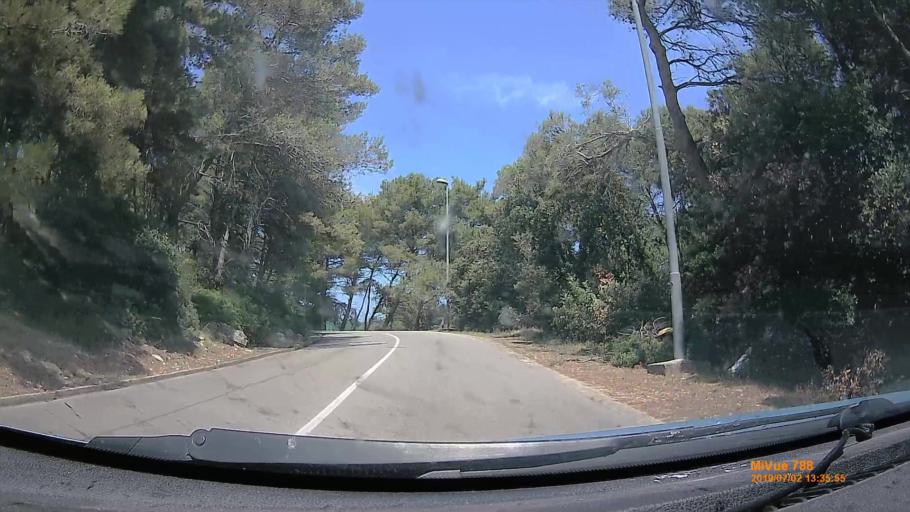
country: HR
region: Primorsko-Goranska
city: Mali Losinj
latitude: 44.5202
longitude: 14.4975
